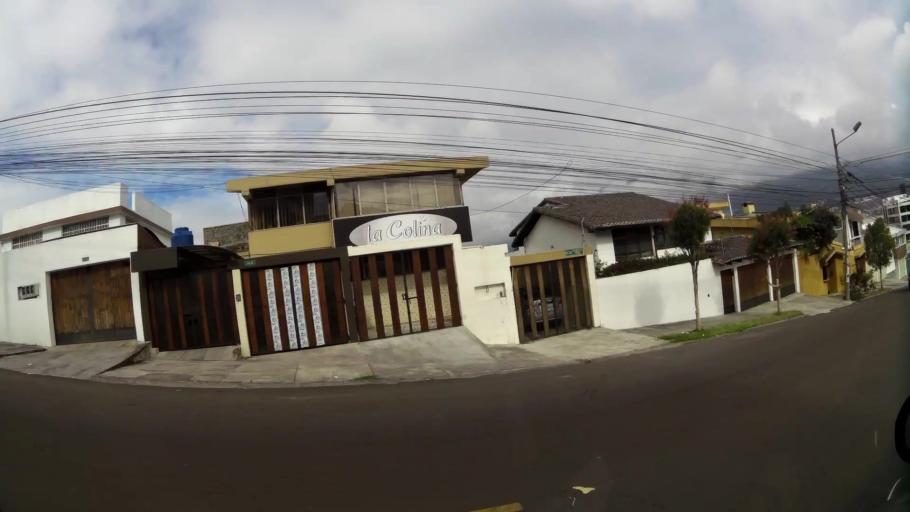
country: EC
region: Pichincha
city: Quito
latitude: -0.1846
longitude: -78.4751
